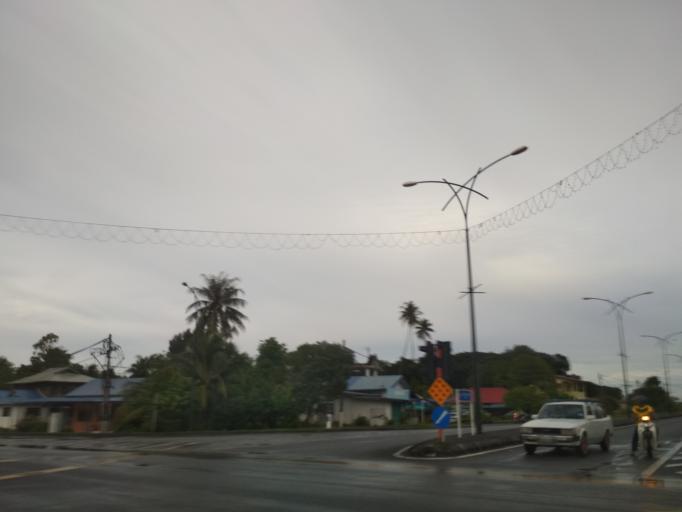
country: MY
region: Perlis
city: Kangar
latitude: 6.4647
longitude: 100.2094
